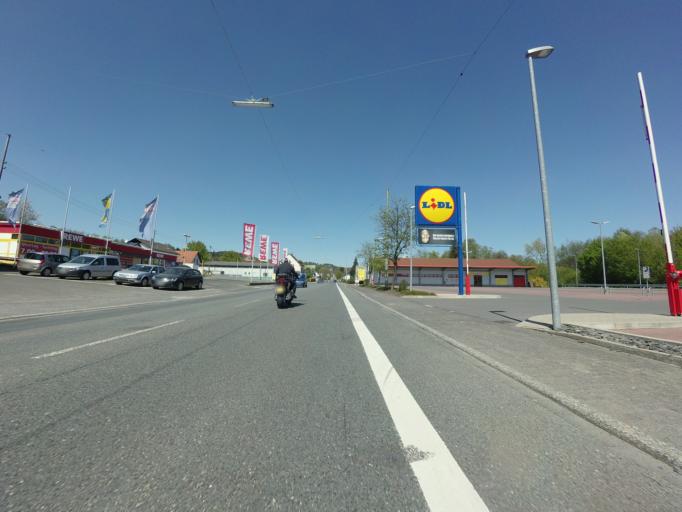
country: DE
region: North Rhine-Westphalia
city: Kreuztal
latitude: 50.9846
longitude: 7.9625
